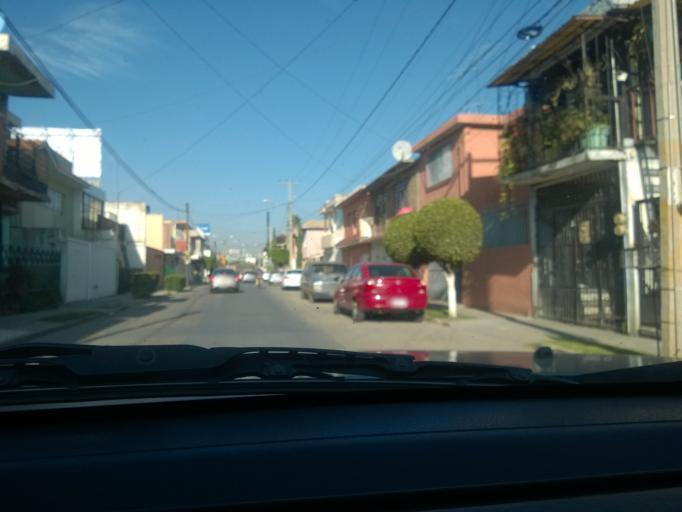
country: MX
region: Guanajuato
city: Leon
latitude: 21.1465
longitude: -101.6707
